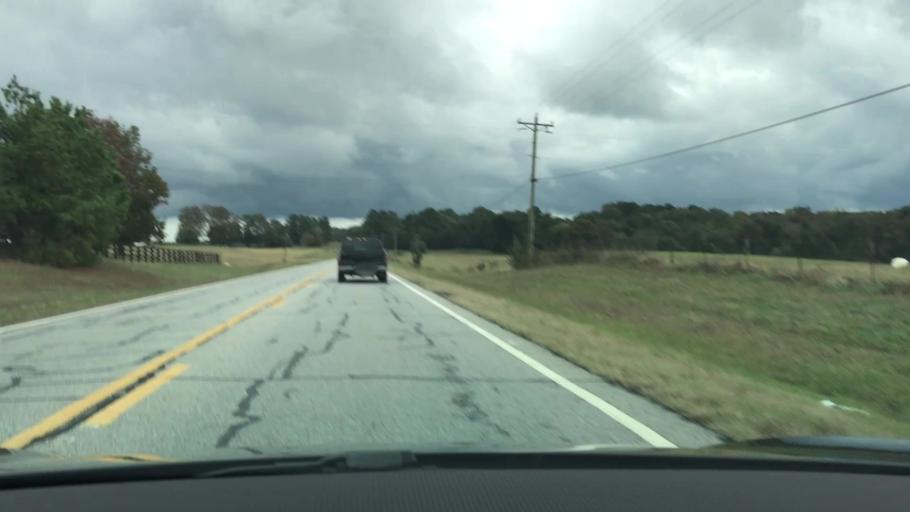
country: US
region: Georgia
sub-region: Oconee County
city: Watkinsville
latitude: 33.7950
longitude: -83.3287
